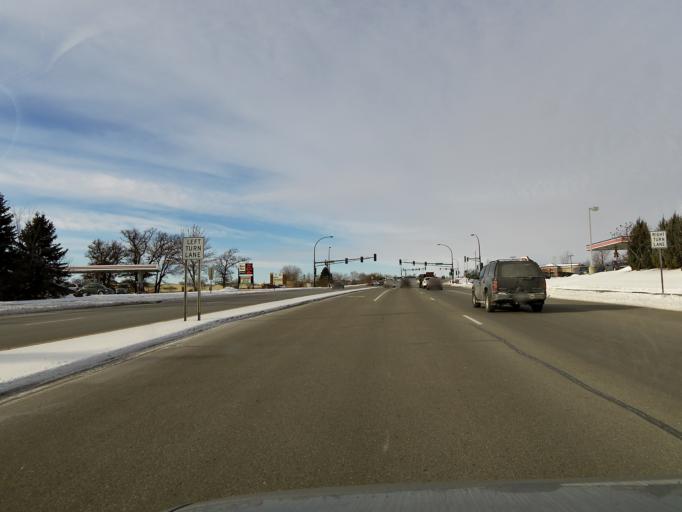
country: US
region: Minnesota
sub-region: Dakota County
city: Burnsville
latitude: 44.7139
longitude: -93.2776
